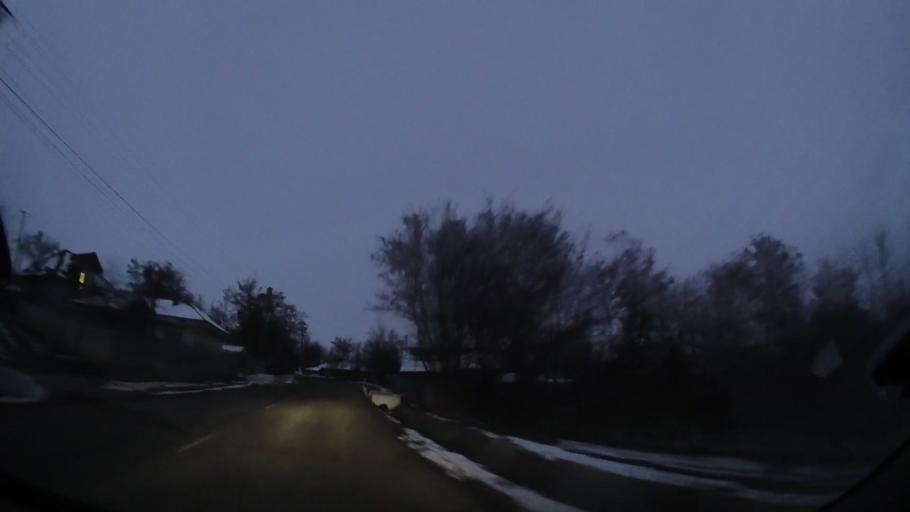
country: RO
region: Vaslui
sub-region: Comuna Dimitrie Cantemir
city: Dimitrie Cantemir
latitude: 46.5073
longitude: 28.0548
